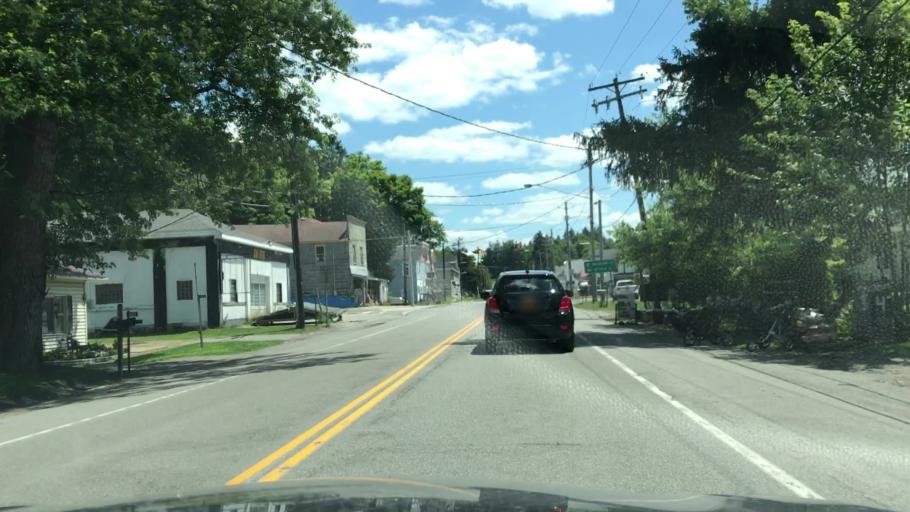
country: US
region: New York
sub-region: Wyoming County
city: Attica
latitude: 42.7627
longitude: -78.3138
